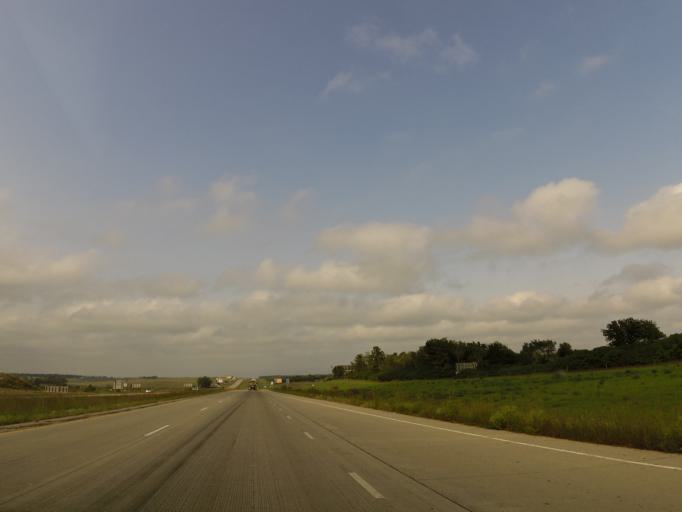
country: US
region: South Dakota
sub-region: Codington County
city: Watertown
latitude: 44.8958
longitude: -97.0565
